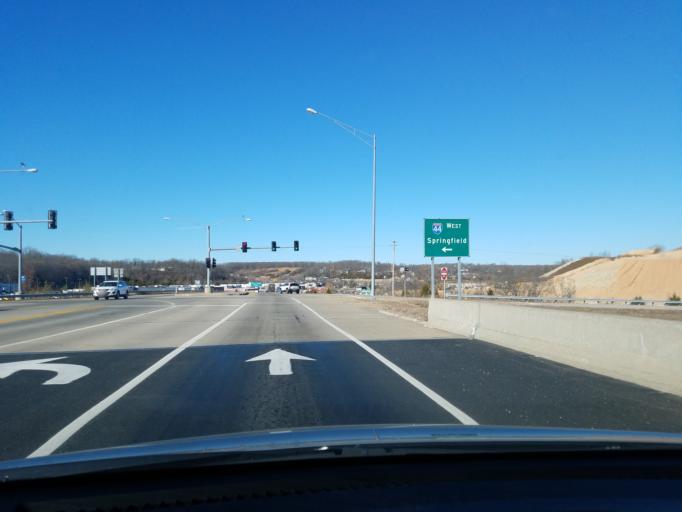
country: US
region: Missouri
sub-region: Pulaski County
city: Waynesville
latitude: 37.8047
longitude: -92.2218
